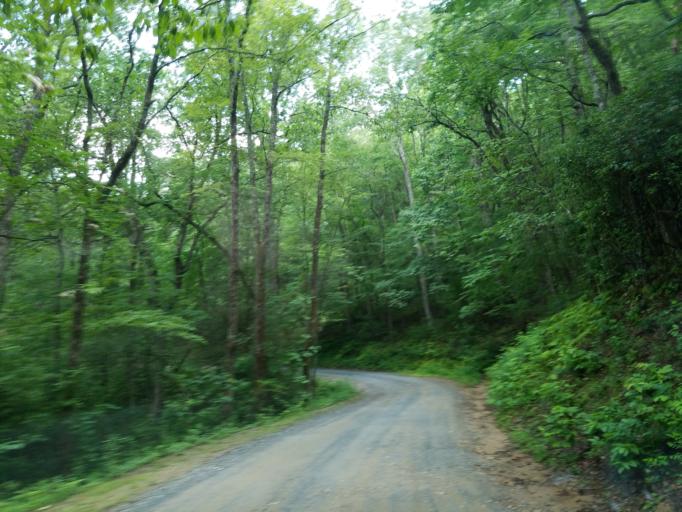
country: US
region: Georgia
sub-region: Fannin County
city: Blue Ridge
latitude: 34.6536
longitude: -84.2169
